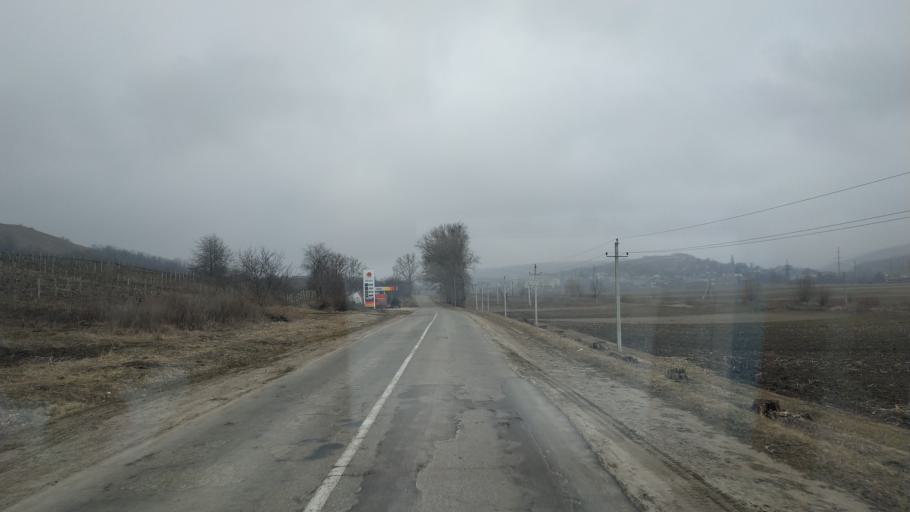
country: MD
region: Hincesti
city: Hincesti
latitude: 46.9708
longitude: 28.4751
